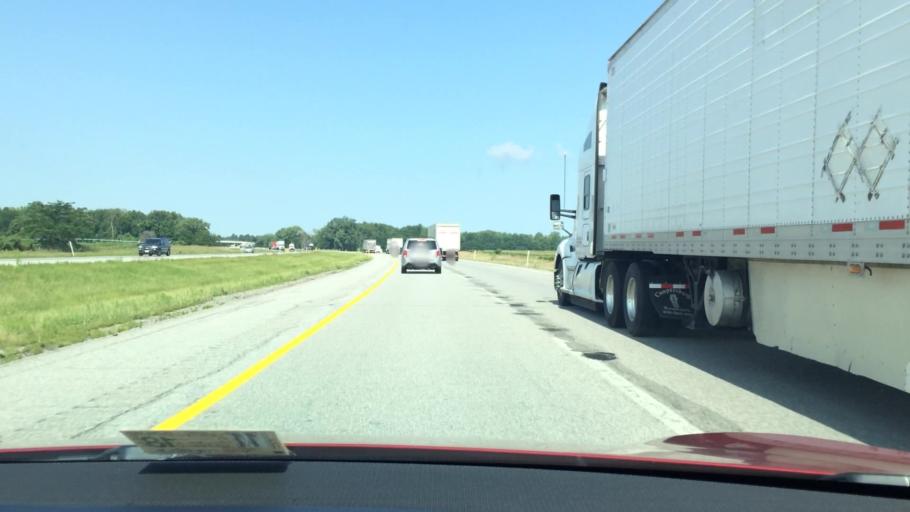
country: US
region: Michigan
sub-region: Saint Joseph County
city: White Pigeon
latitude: 41.7533
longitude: -85.5714
